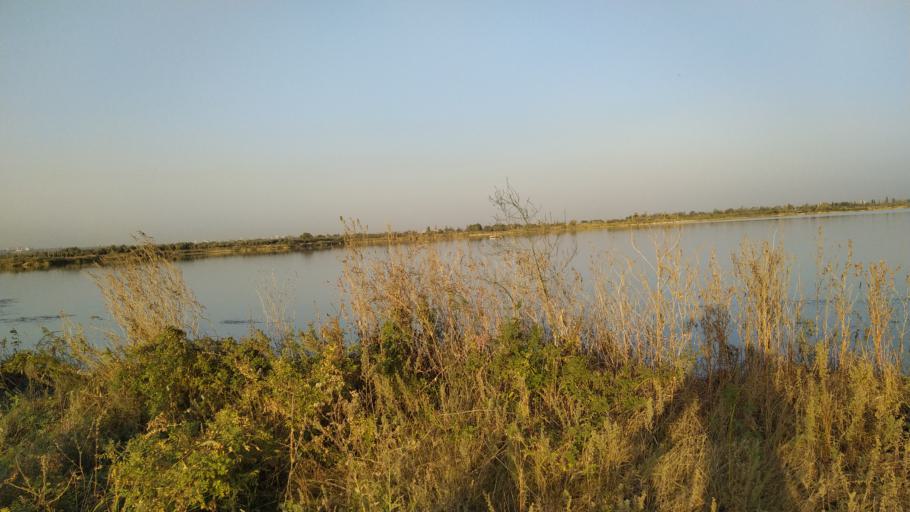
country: RU
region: Rostov
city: Bataysk
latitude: 47.1443
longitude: 39.6475
